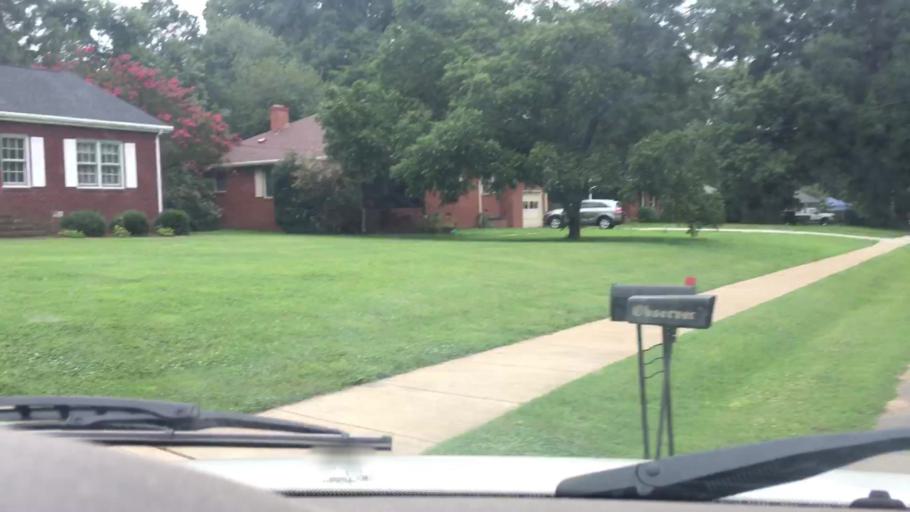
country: US
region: North Carolina
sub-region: Mecklenburg County
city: Cornelius
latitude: 35.4924
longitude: -80.8591
